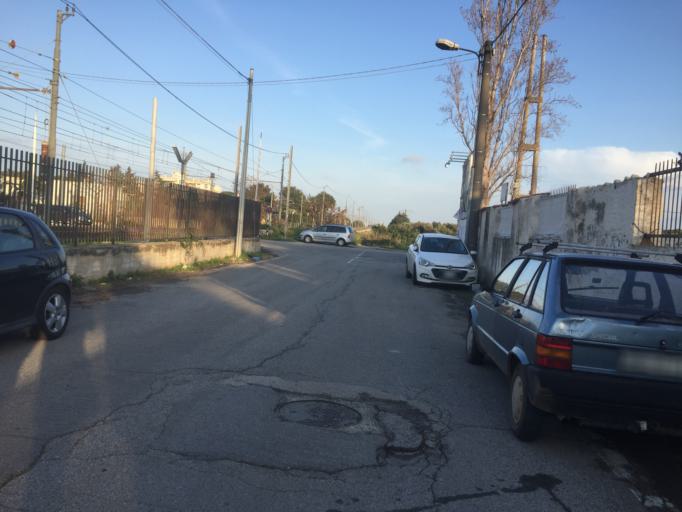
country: IT
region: Apulia
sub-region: Provincia di Bari
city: Parco Scizzo-Parchitello
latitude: 41.0822
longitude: 16.9969
